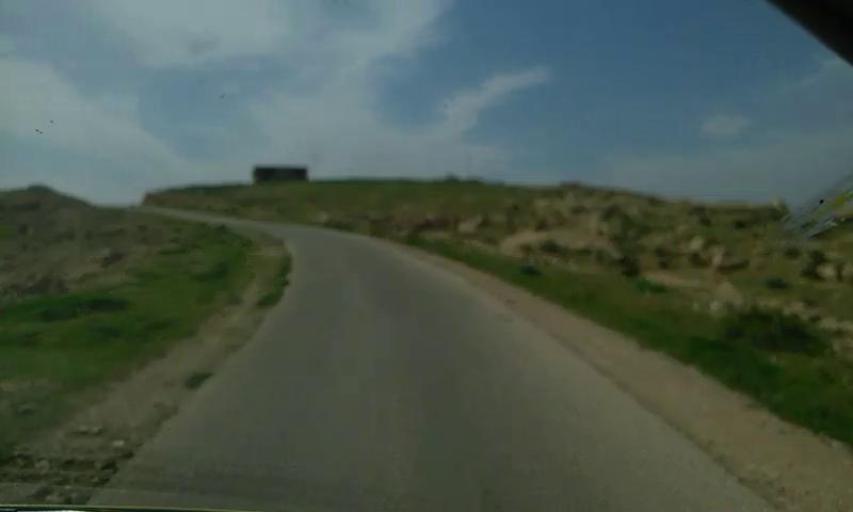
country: PS
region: West Bank
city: Khallat al Mayyah
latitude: 31.4415
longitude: 35.2033
